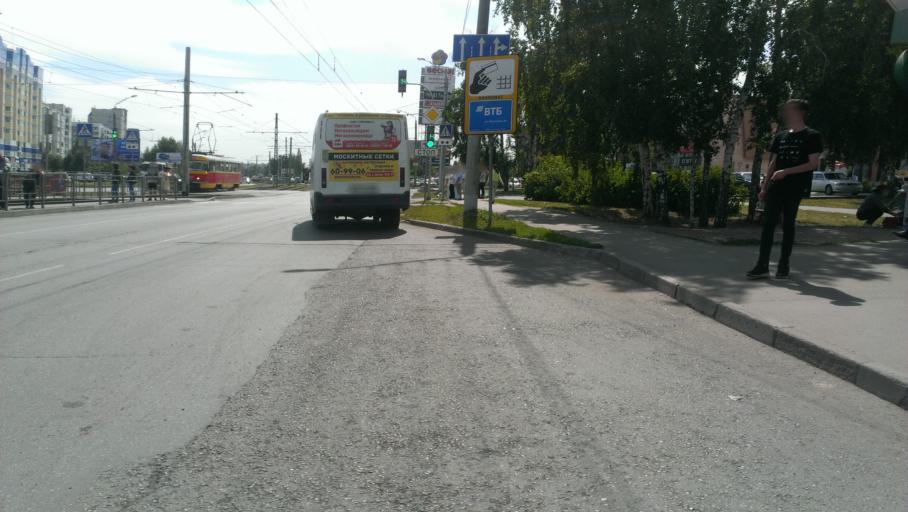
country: RU
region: Altai Krai
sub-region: Gorod Barnaulskiy
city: Barnaul
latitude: 53.3579
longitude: 83.6993
